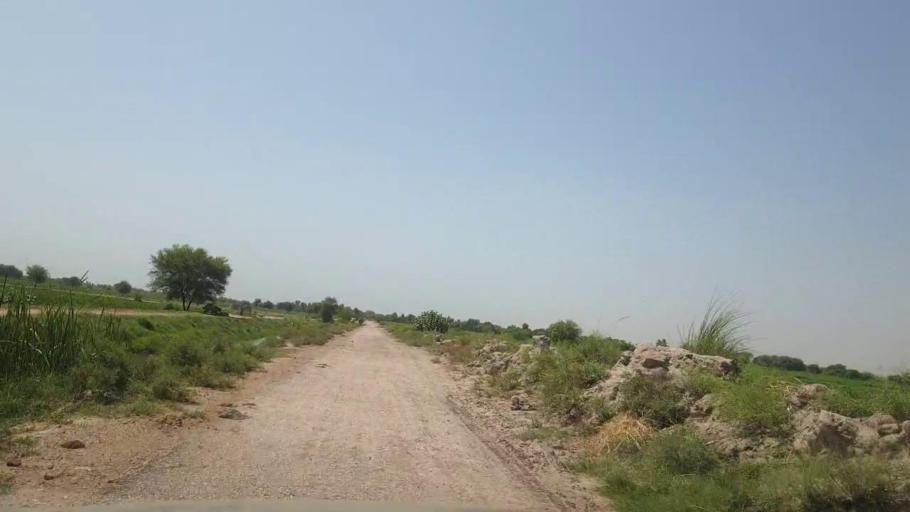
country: PK
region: Sindh
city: Rohri
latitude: 27.6626
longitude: 68.9810
